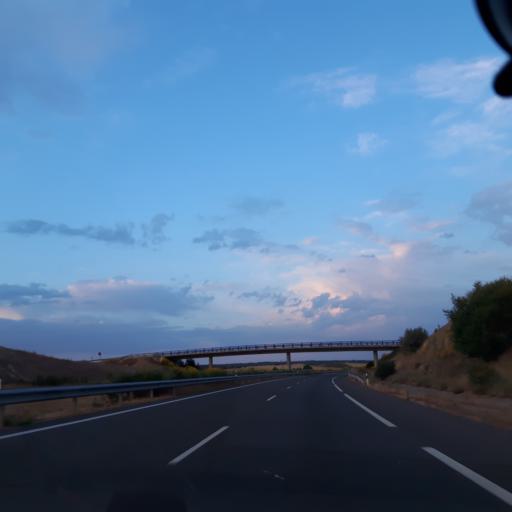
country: ES
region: Castille and Leon
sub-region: Provincia de Salamanca
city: Mozarbez
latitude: 40.8570
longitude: -5.6415
